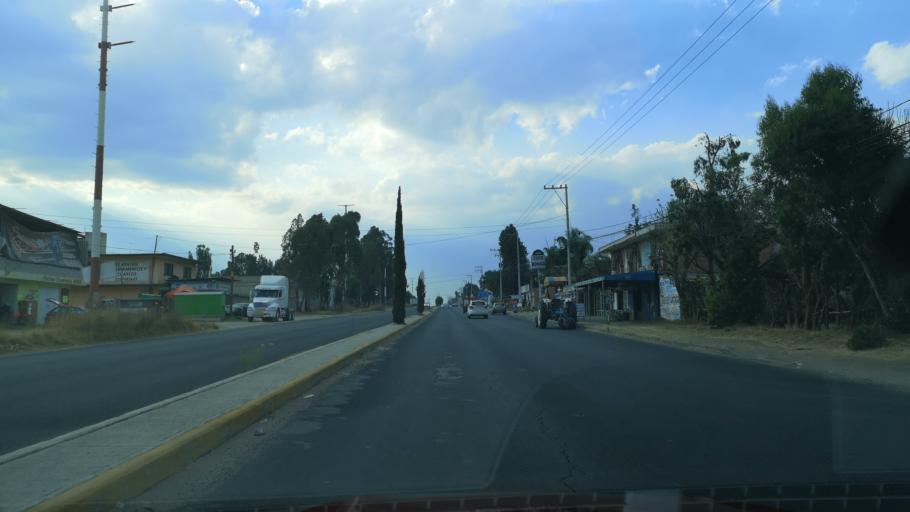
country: MX
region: Puebla
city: Cuanala
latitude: 19.1032
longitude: -98.3476
